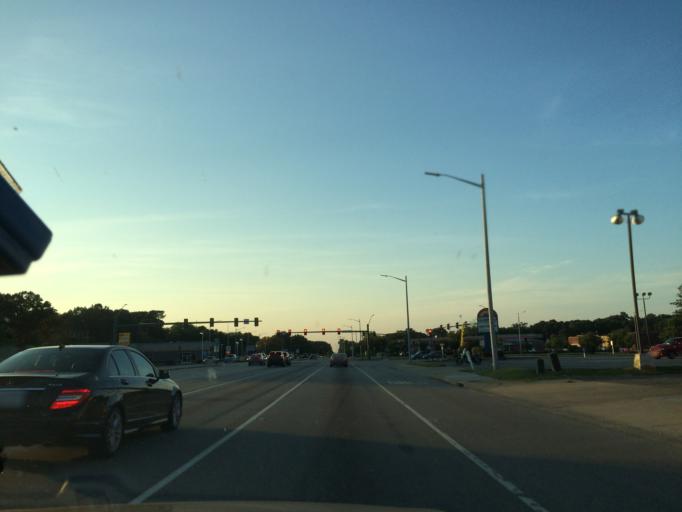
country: US
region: Virginia
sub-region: City of Newport News
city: Newport News
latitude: 37.0585
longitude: -76.4652
